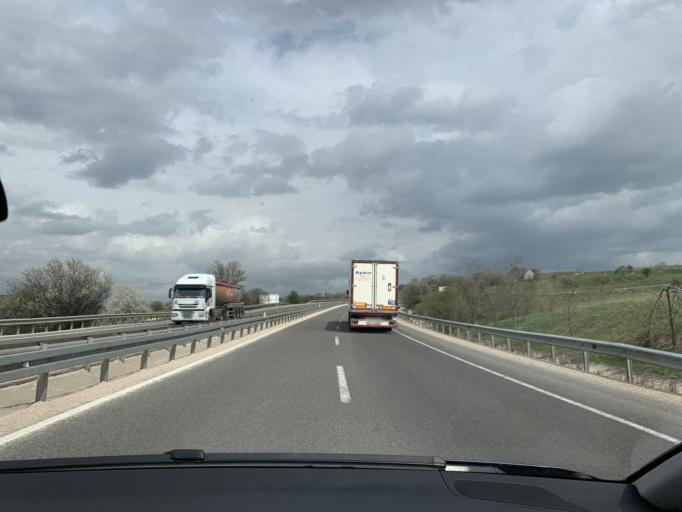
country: TR
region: Bolu
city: Yenicaga
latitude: 40.7827
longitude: 32.0798
